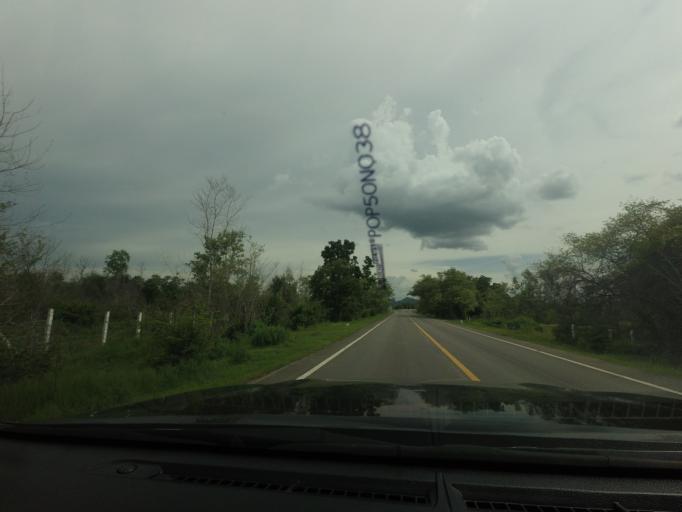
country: TH
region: Kanchanaburi
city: Kanchanaburi
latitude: 14.1146
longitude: 99.4102
